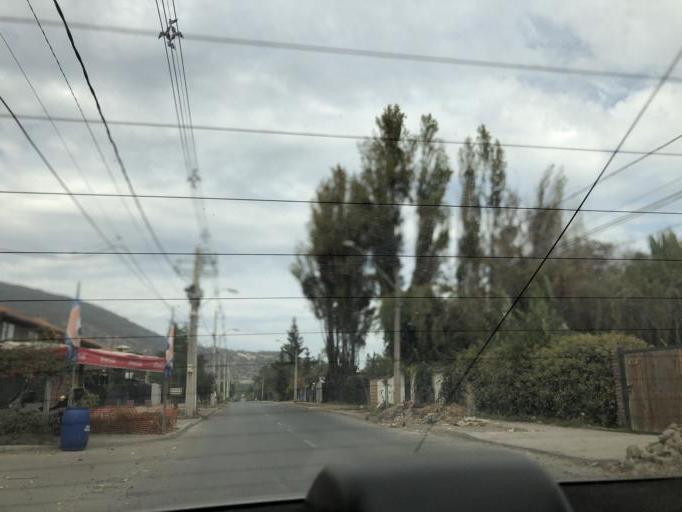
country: CL
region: Santiago Metropolitan
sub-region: Provincia de Cordillera
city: Puente Alto
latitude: -33.6109
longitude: -70.5308
